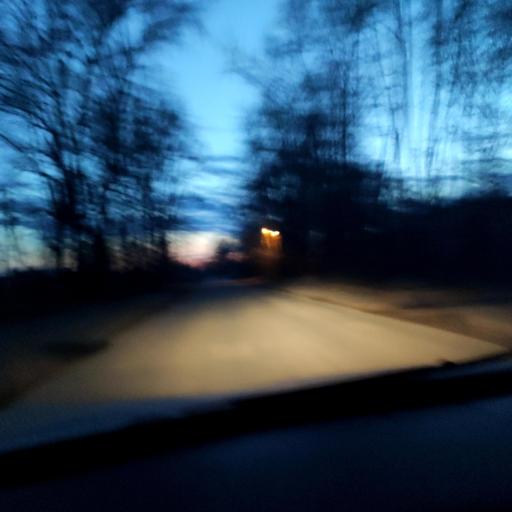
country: RU
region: Perm
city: Overyata
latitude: 58.0334
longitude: 55.8434
